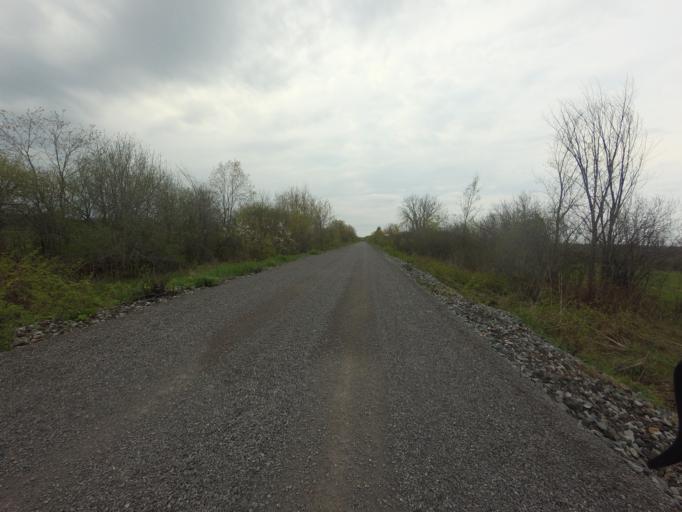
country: CA
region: Ontario
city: Carleton Place
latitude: 45.2145
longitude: -76.1808
